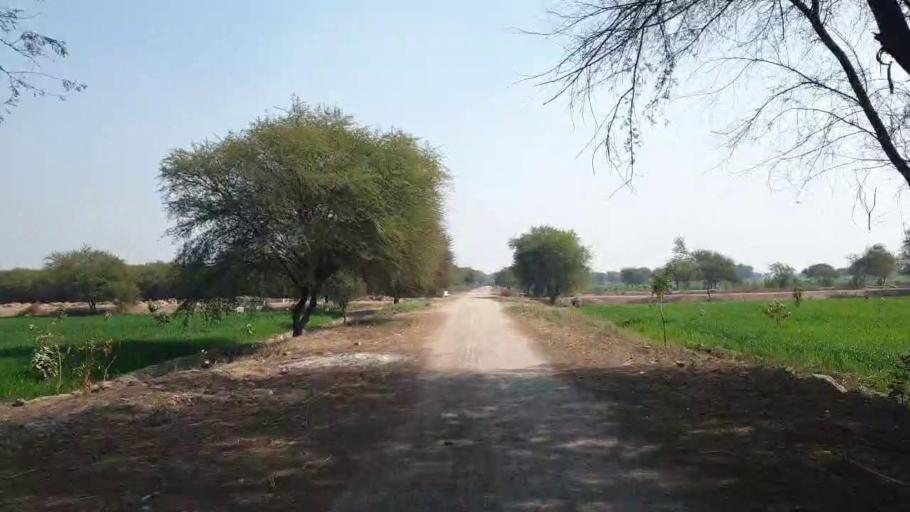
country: PK
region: Sindh
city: Chambar
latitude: 25.3521
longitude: 68.9267
